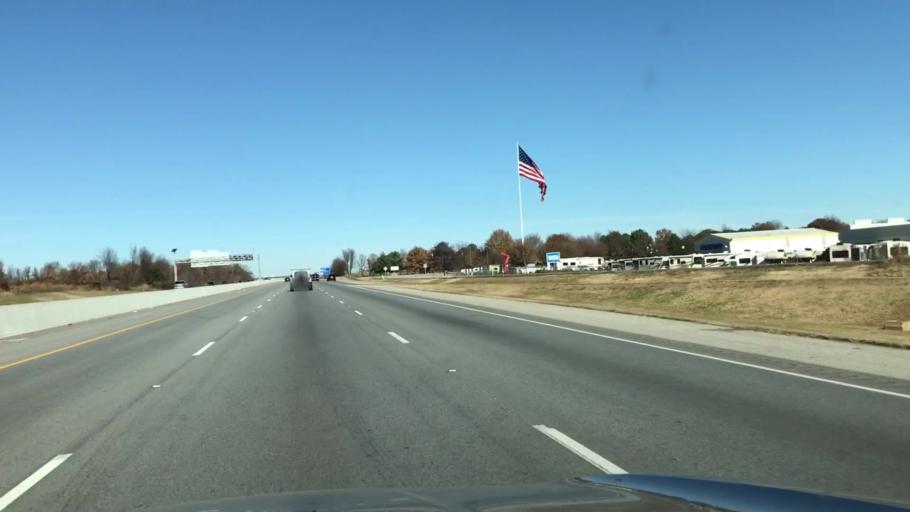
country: US
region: Arkansas
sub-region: Benton County
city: Lowell
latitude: 36.2575
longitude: -94.1503
